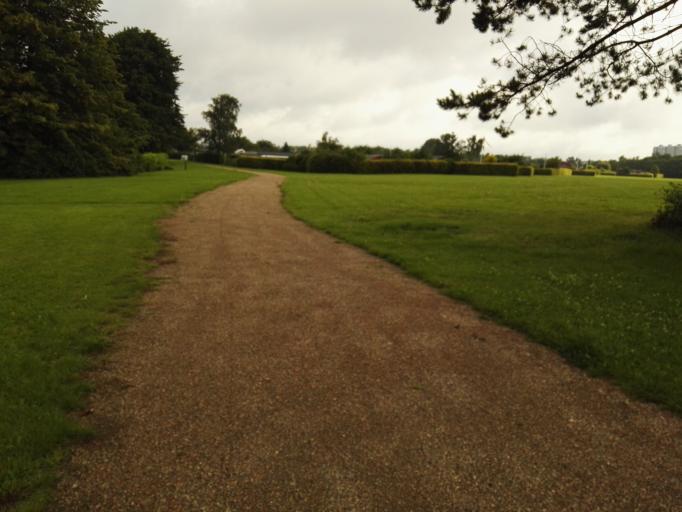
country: DK
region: Capital Region
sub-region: Ballerup Kommune
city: Ballerup
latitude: 55.7118
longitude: 12.3470
